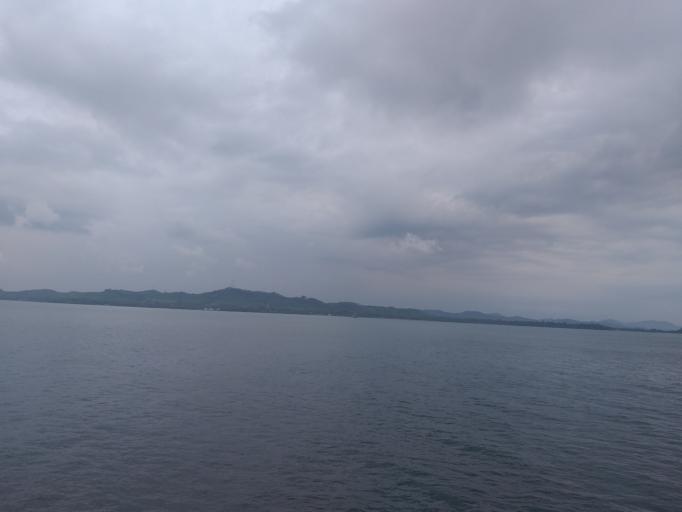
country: TH
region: Trat
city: Laem Ngop
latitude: 12.1605
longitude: 102.2915
